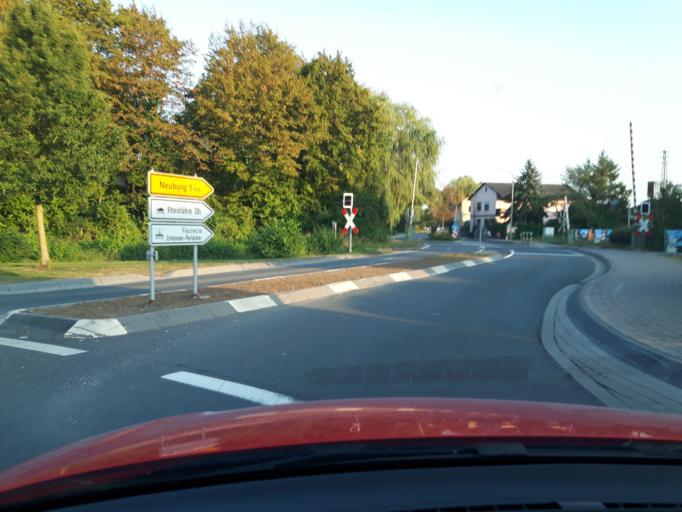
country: DE
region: Rheinland-Pfalz
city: Hagenbach
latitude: 49.0171
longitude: 8.2533
